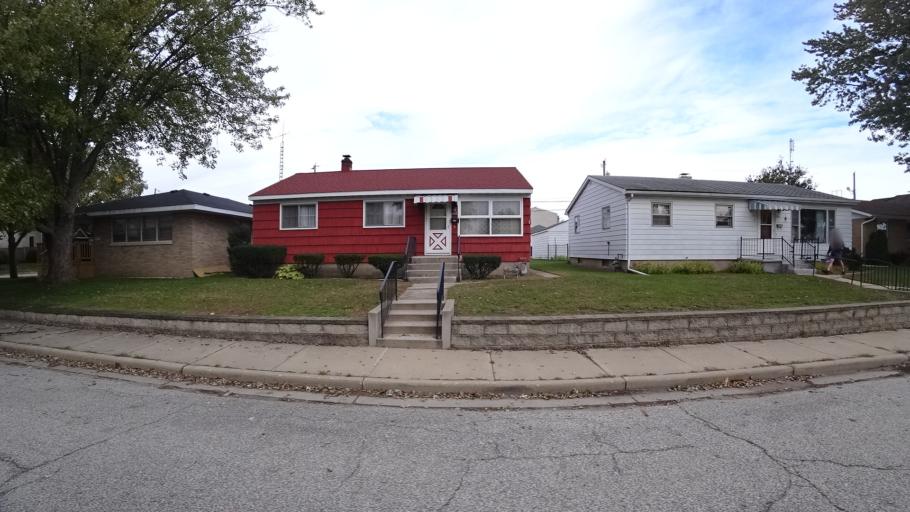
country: US
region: Indiana
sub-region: LaPorte County
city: Michigan City
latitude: 41.7042
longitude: -86.8982
